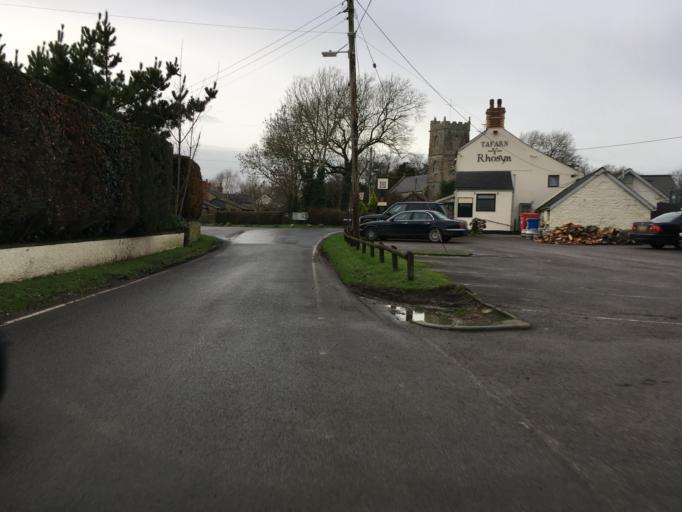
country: GB
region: Wales
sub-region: Newport
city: Redwick
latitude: 51.5528
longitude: -2.8476
